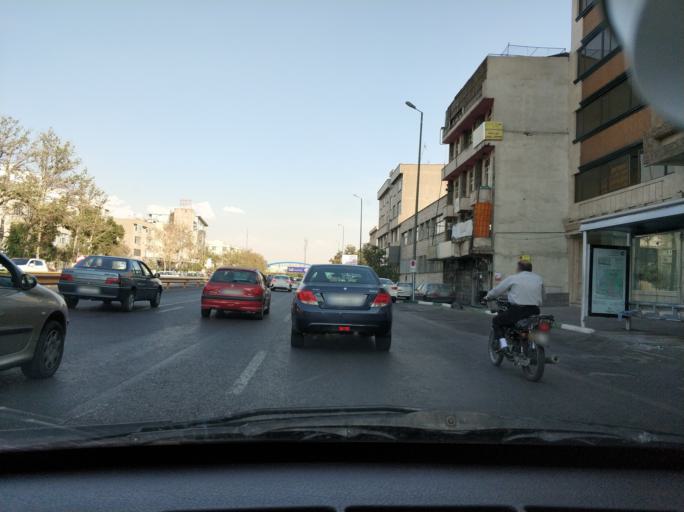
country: IR
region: Tehran
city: Tehran
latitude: 35.7414
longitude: 51.4538
